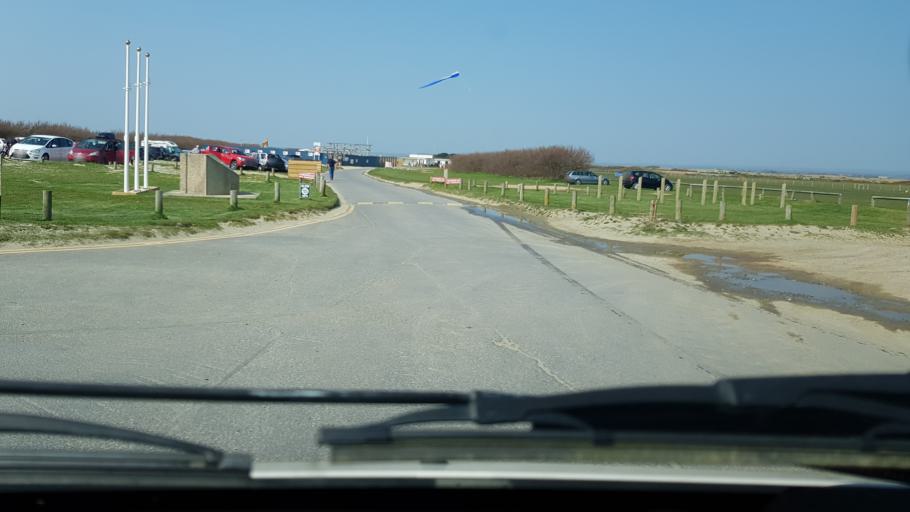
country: GB
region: England
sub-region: West Sussex
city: East Wittering
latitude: 50.7755
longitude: -0.9063
